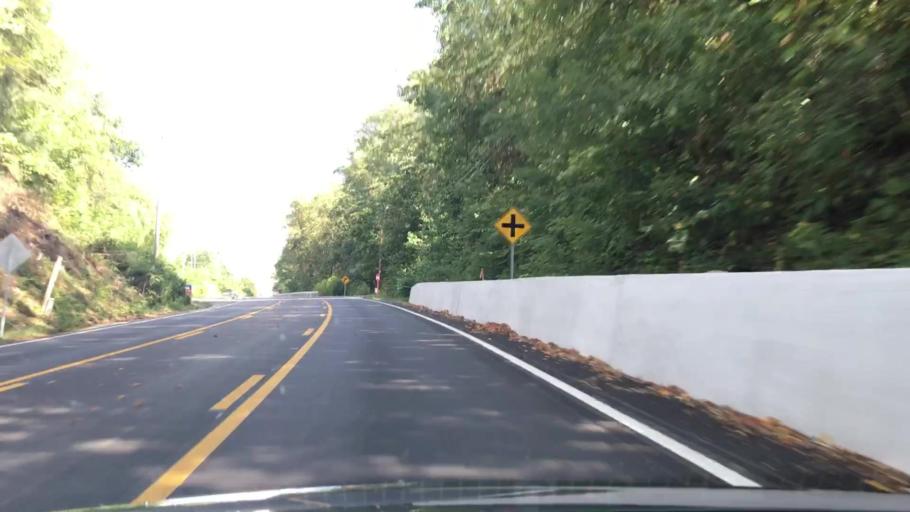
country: US
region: Alabama
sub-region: Limestone County
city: Ardmore
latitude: 35.0019
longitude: -86.8677
